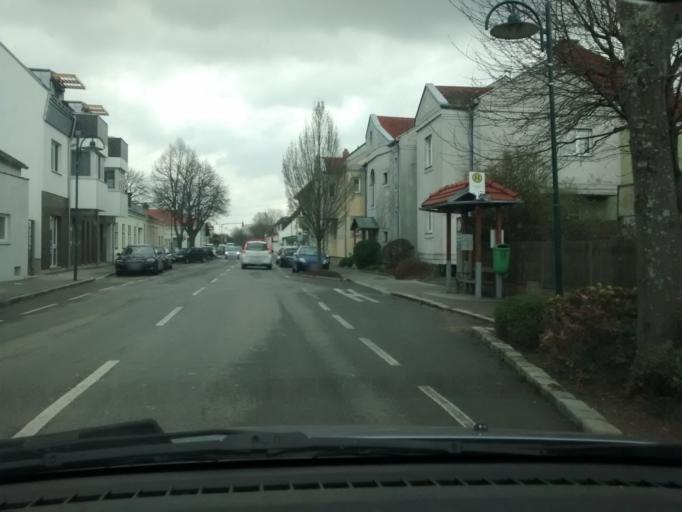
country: AT
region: Lower Austria
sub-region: Politischer Bezirk Modling
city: Biedermannsdorf
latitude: 48.0830
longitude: 16.3511
